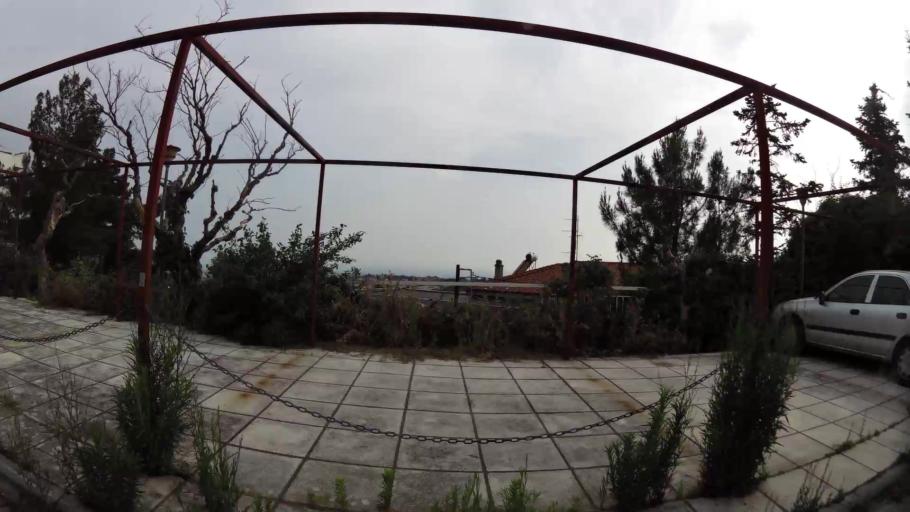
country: GR
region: Central Macedonia
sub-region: Nomos Thessalonikis
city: Oraiokastro
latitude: 40.7325
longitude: 22.9230
